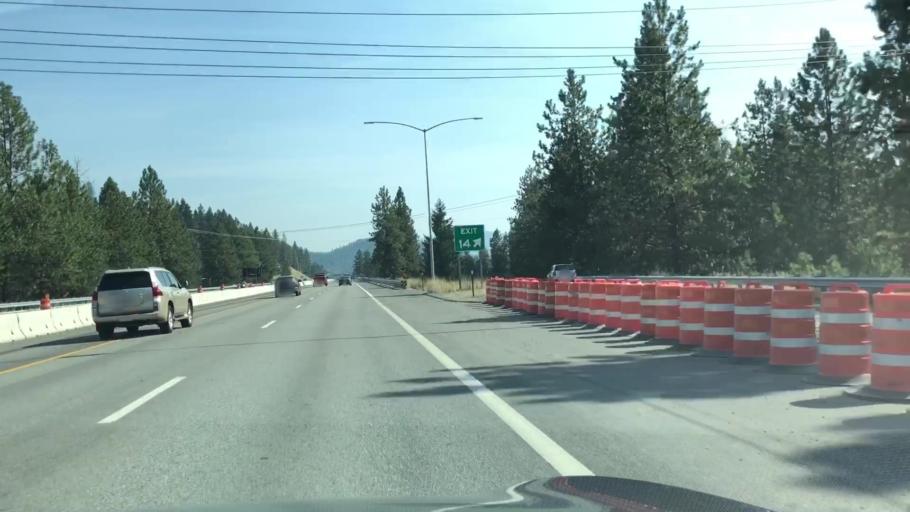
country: US
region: Idaho
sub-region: Kootenai County
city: Coeur d'Alene
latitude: 47.6904
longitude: -116.7667
